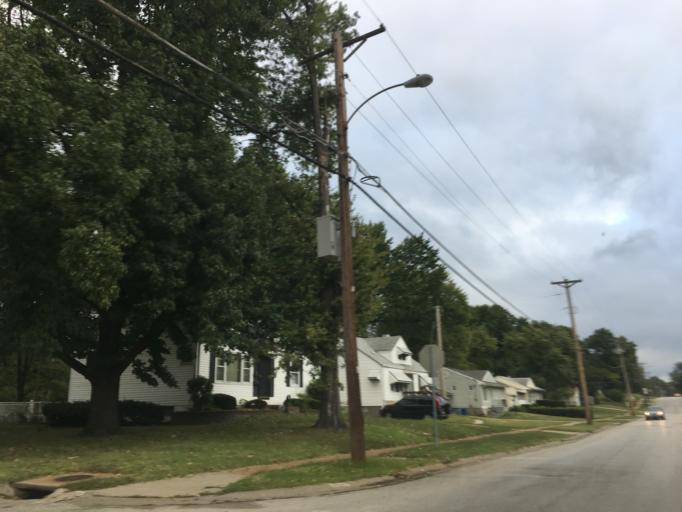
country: US
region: Missouri
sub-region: Saint Louis County
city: Berkeley
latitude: 38.7623
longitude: -90.3337
